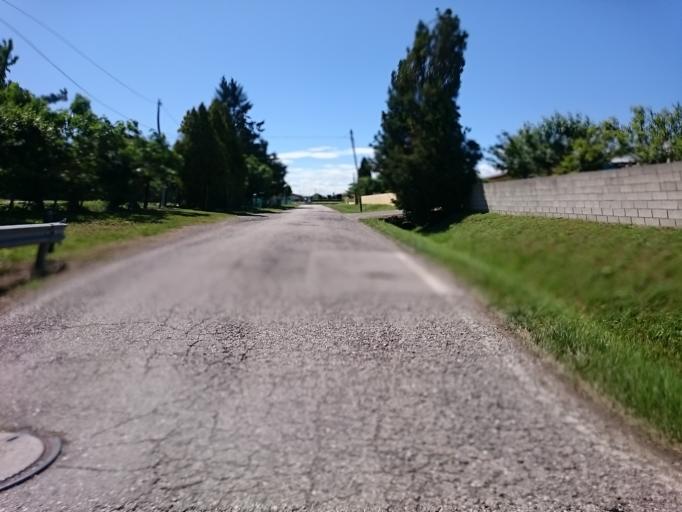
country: IT
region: Veneto
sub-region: Provincia di Padova
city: Codevigo
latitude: 45.2673
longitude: 12.0908
